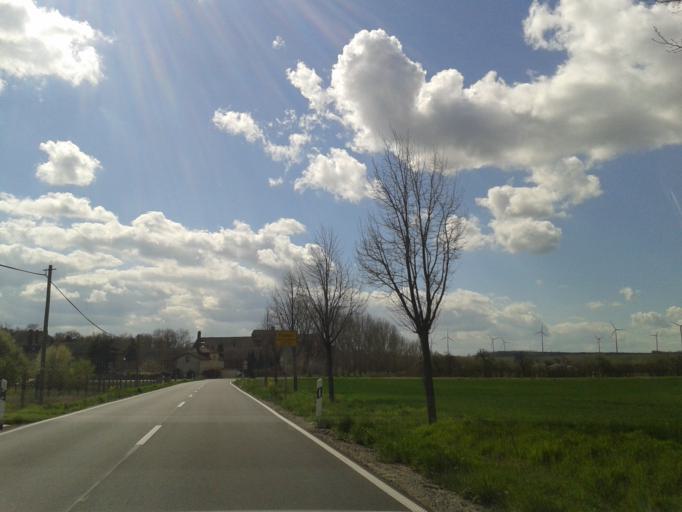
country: DE
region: Saxony-Anhalt
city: Wansleben
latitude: 51.4338
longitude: 11.7619
